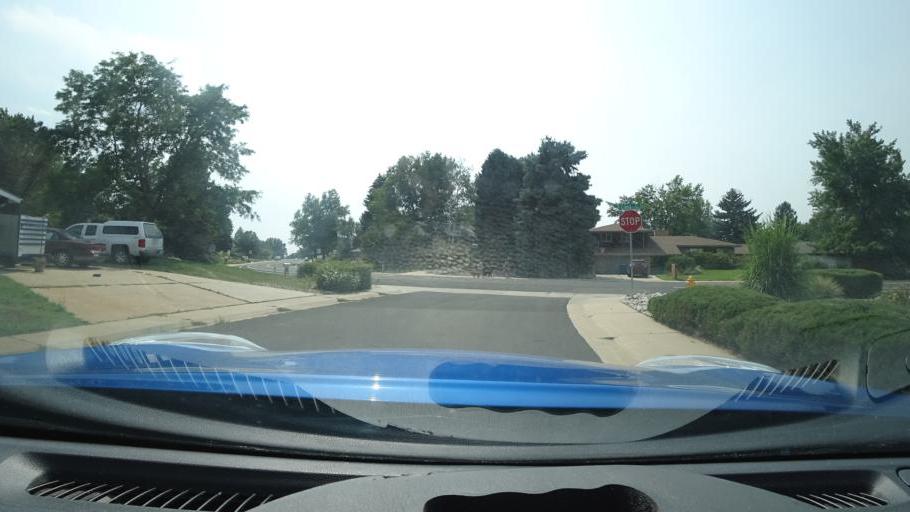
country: US
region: Colorado
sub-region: Adams County
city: Aurora
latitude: 39.6727
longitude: -104.8558
